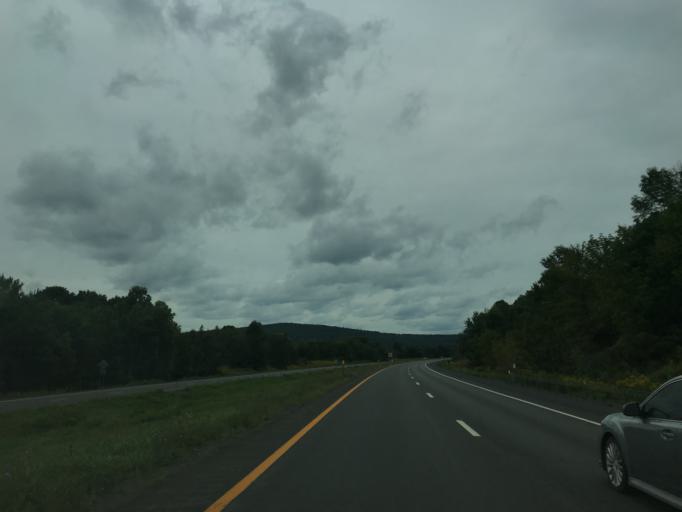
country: US
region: New York
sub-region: Delaware County
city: Sidney
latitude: 42.3056
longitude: -75.3756
